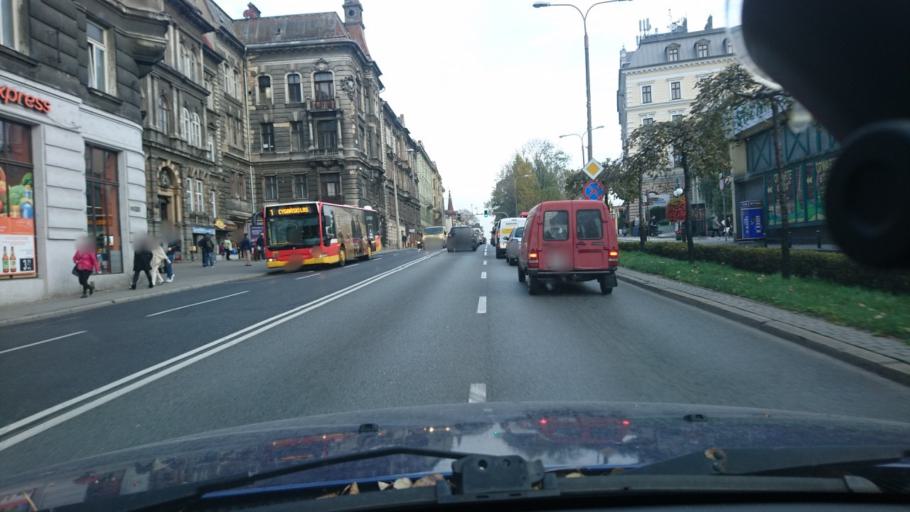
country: PL
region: Silesian Voivodeship
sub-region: Bielsko-Biala
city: Bielsko-Biala
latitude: 49.8230
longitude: 19.0450
